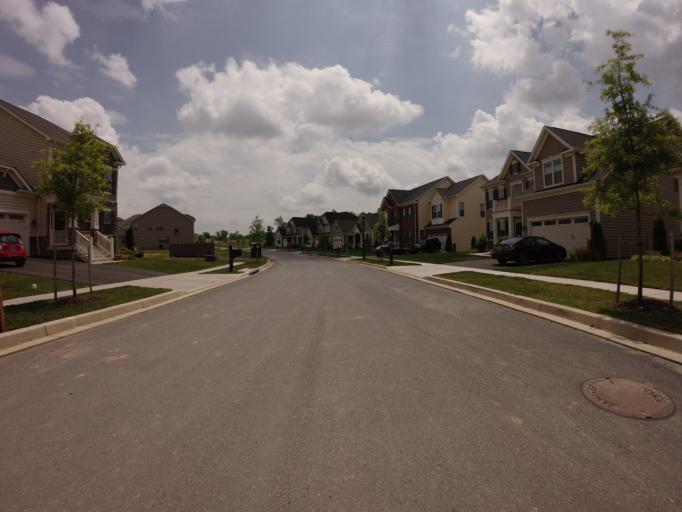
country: US
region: Maryland
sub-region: Frederick County
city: Brunswick
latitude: 39.3256
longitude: -77.6332
